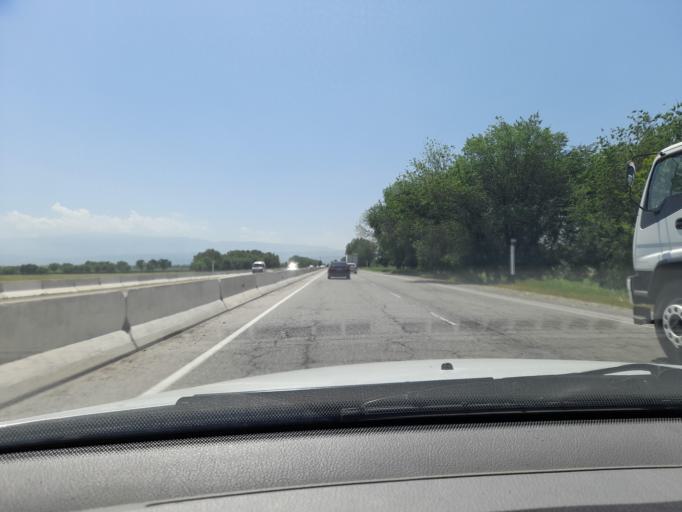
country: UZ
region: Jizzax
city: Jizzax
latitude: 40.1176
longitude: 67.9470
